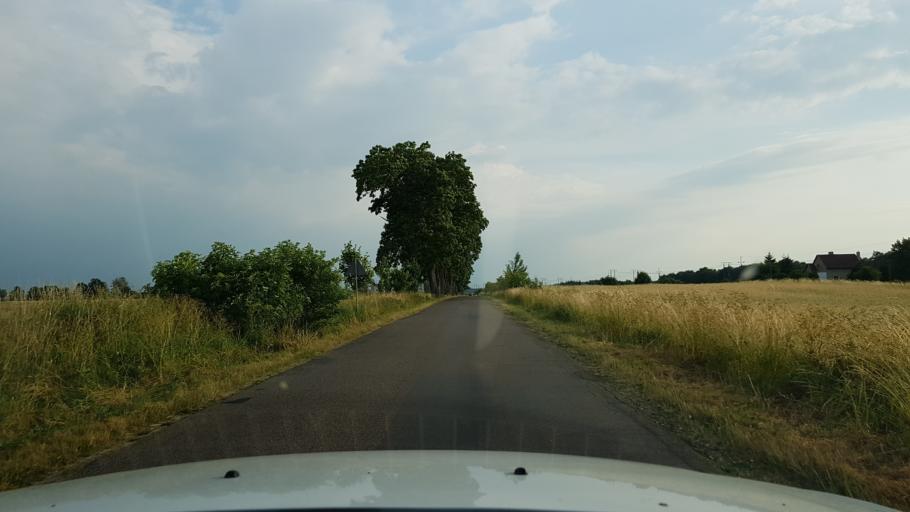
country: PL
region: West Pomeranian Voivodeship
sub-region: Powiat swidwinski
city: Swidwin
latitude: 53.8054
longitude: 15.7913
